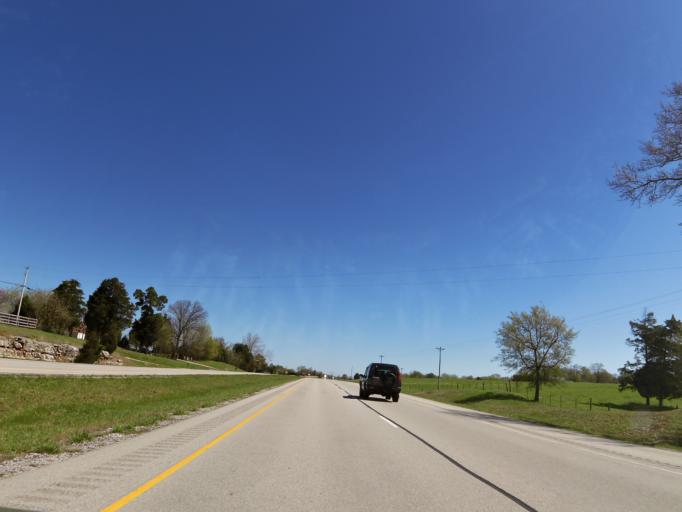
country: US
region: Kentucky
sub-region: Logan County
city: Auburn
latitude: 36.9107
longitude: -86.5790
